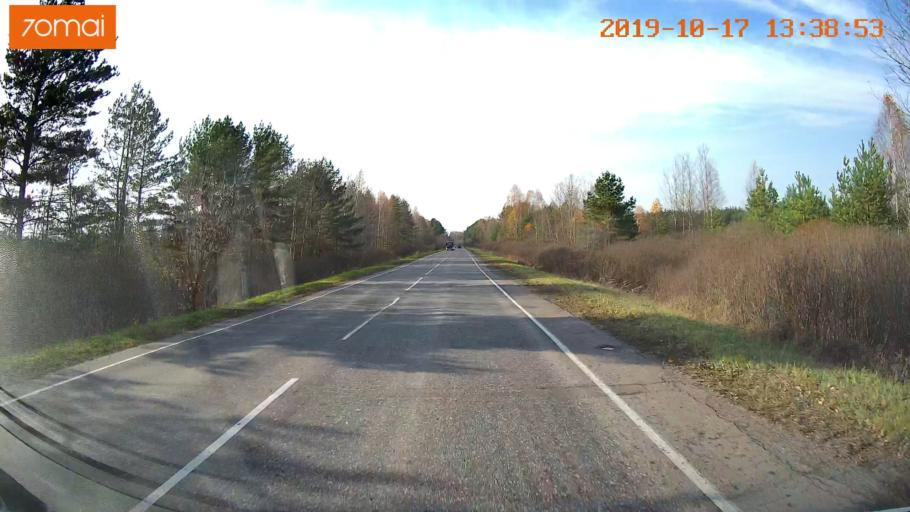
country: RU
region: Rjazan
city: Tuma
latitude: 55.1450
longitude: 40.6019
